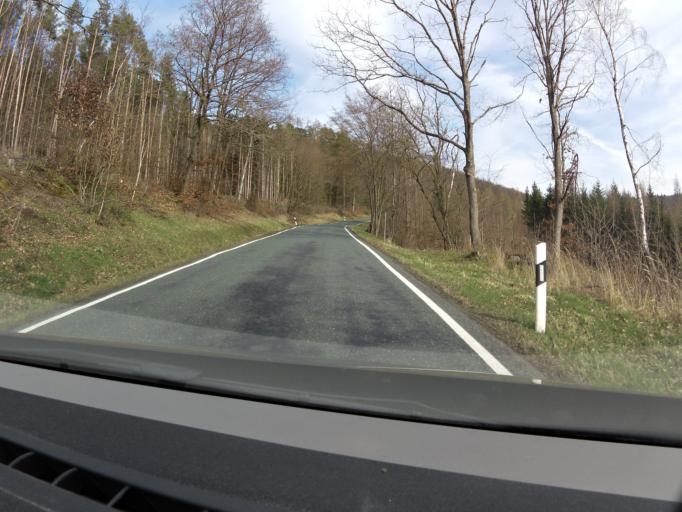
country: DE
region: Thuringia
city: Stadtlengsfeld
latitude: 50.7949
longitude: 10.1342
